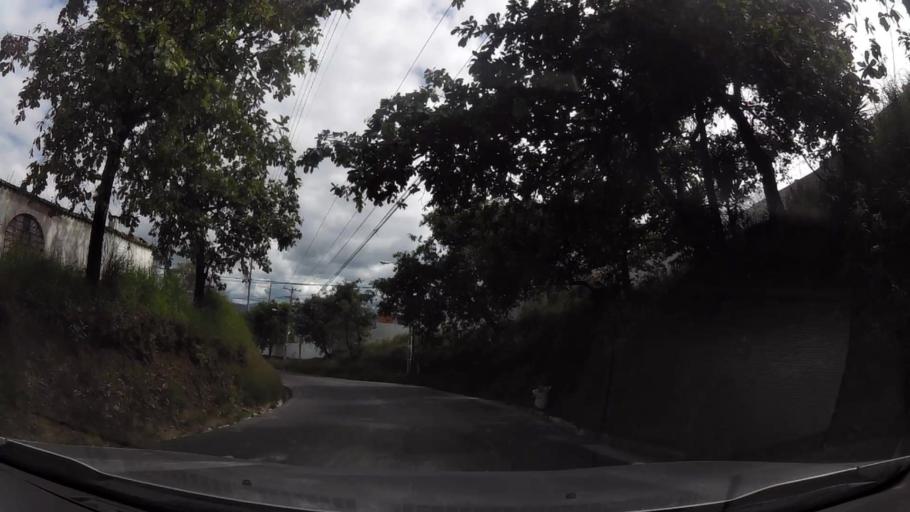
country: GT
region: Guatemala
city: Guatemala City
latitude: 14.6740
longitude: -90.5494
